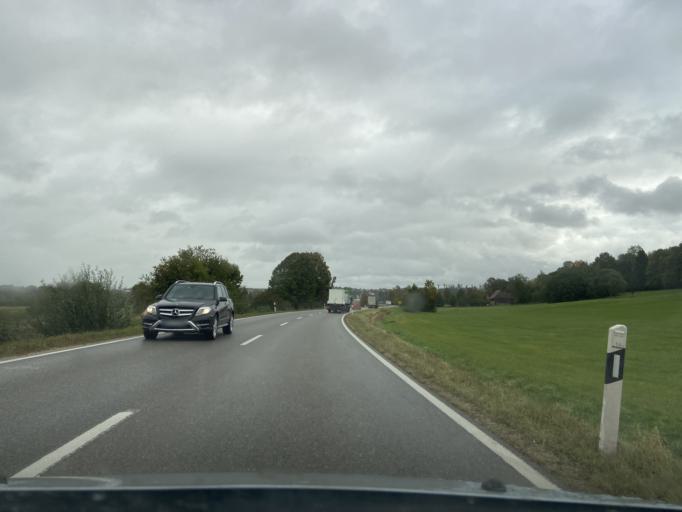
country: DE
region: Baden-Wuerttemberg
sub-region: Tuebingen Region
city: Krauchenwies
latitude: 48.0145
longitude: 9.2229
